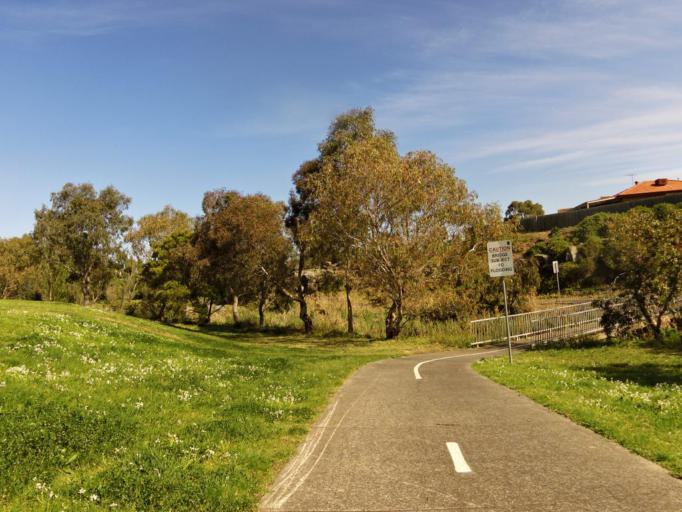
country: AU
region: Victoria
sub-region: Brimbank
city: Sunshine West
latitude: -37.7964
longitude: 144.8218
